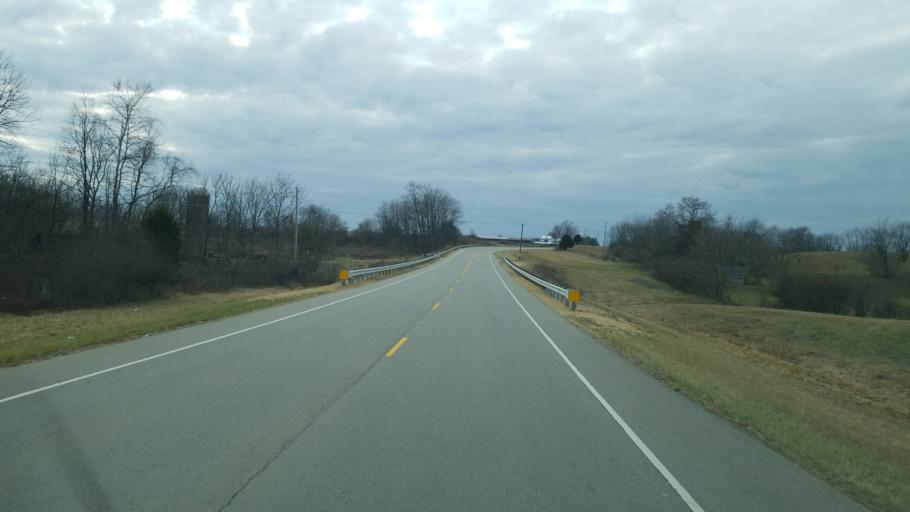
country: US
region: Ohio
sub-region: Highland County
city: Greenfield
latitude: 39.2233
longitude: -83.3983
